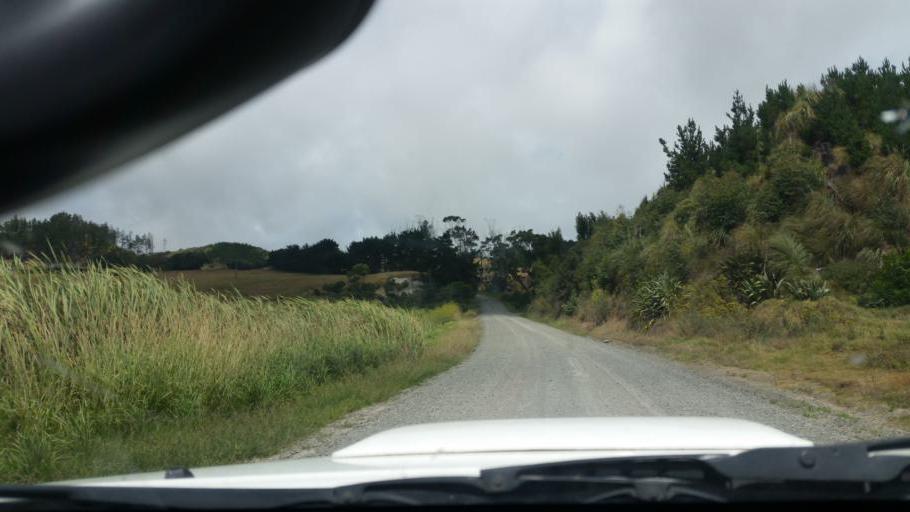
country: NZ
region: Northland
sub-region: Kaipara District
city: Dargaville
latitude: -35.8357
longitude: 173.6609
